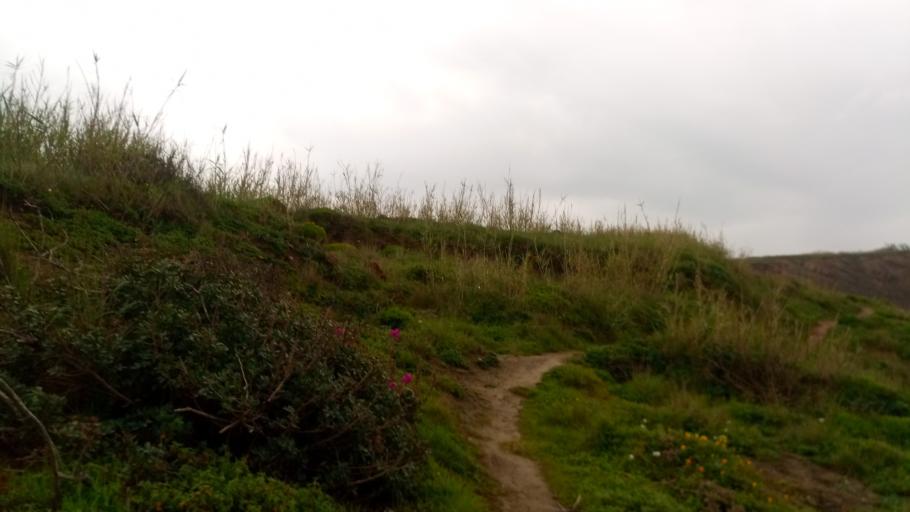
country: PT
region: Leiria
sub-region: Caldas da Rainha
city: Caldas da Rainha
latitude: 39.4702
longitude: -9.2008
